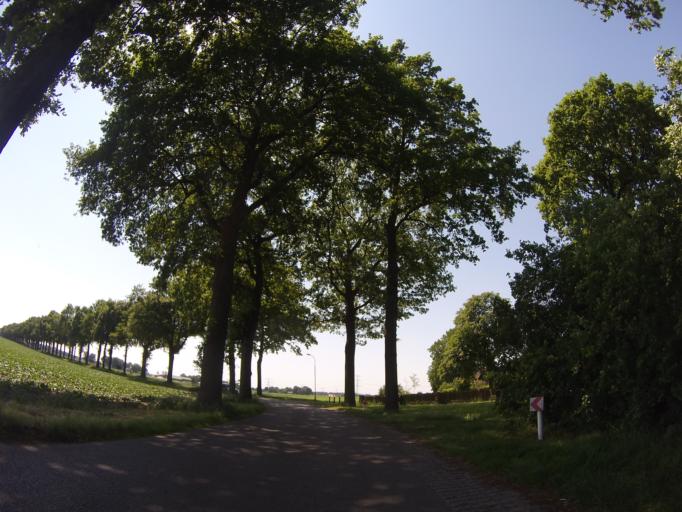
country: NL
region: Drenthe
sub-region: Gemeente Coevorden
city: Sleen
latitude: 52.7417
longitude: 6.8479
